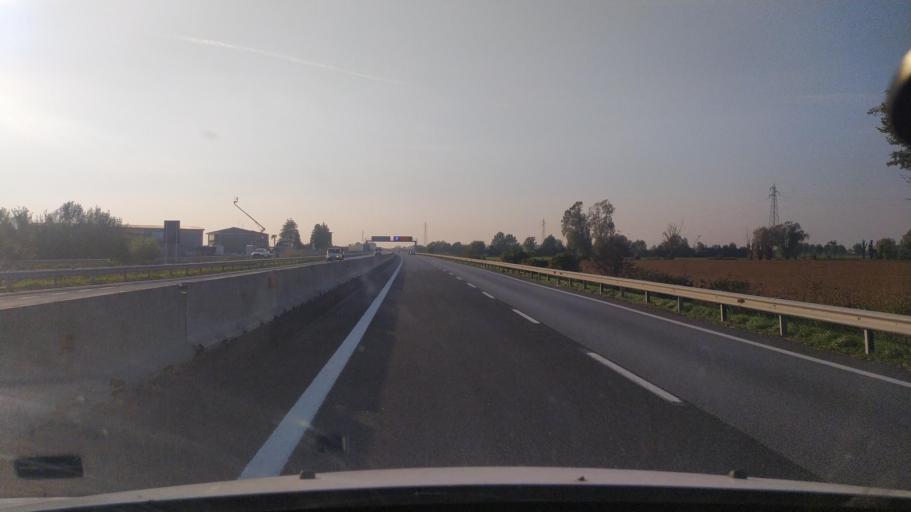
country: IT
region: Lombardy
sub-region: Provincia di Cremona
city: Nosadello
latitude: 45.3874
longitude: 9.5371
